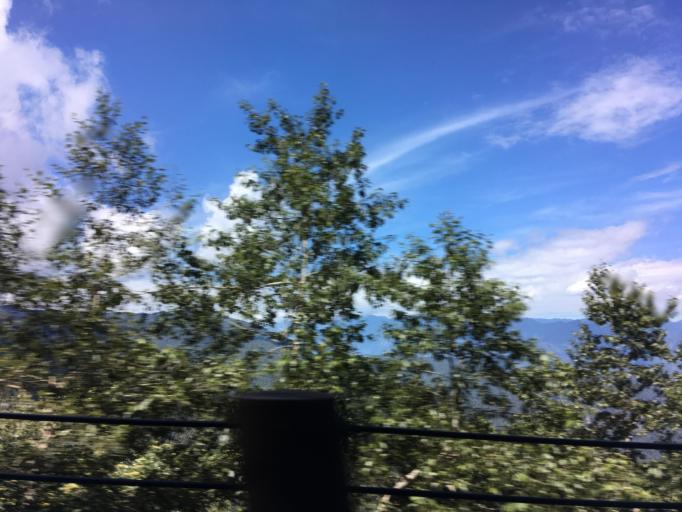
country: TW
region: Taiwan
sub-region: Yilan
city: Yilan
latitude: 24.5090
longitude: 121.5244
